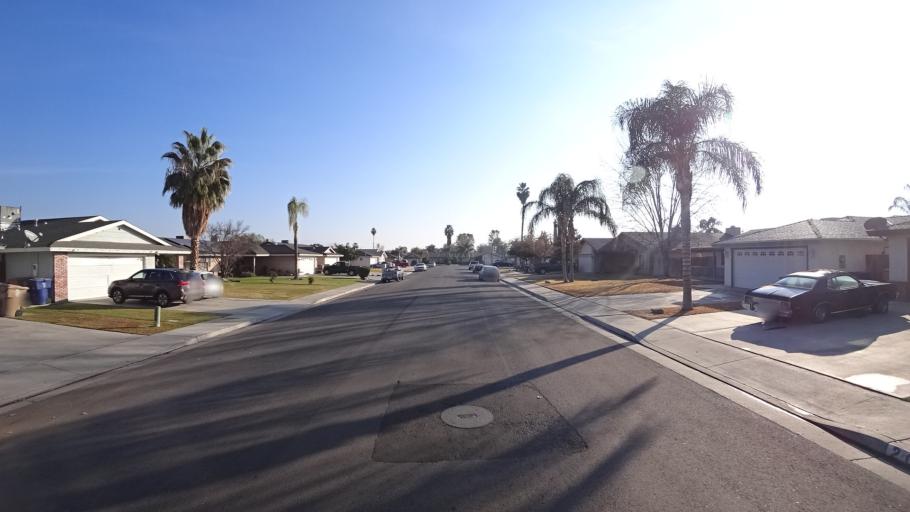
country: US
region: California
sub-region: Kern County
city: Greenfield
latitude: 35.3046
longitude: -119.0253
